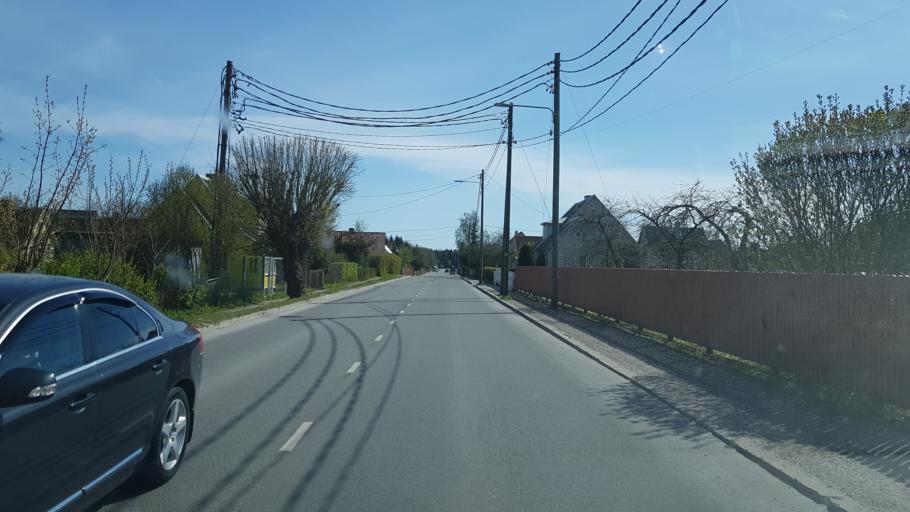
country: EE
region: Harju
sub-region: Keila linn
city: Keila
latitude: 59.3038
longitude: 24.4255
